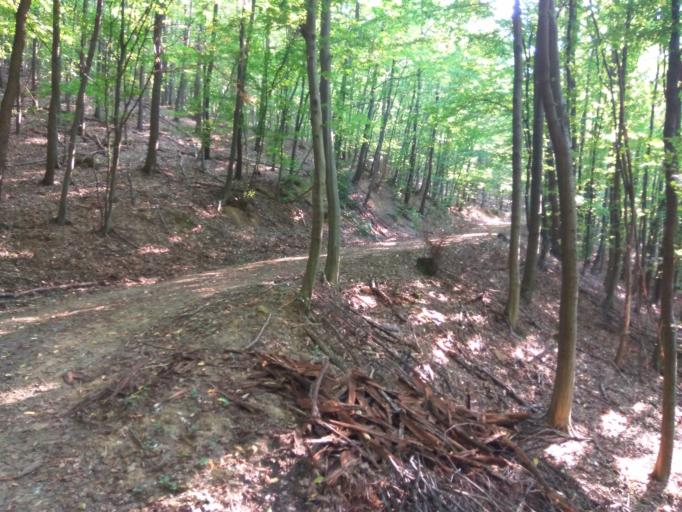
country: HU
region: Heves
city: Paradsasvar
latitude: 47.9213
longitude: 19.9740
